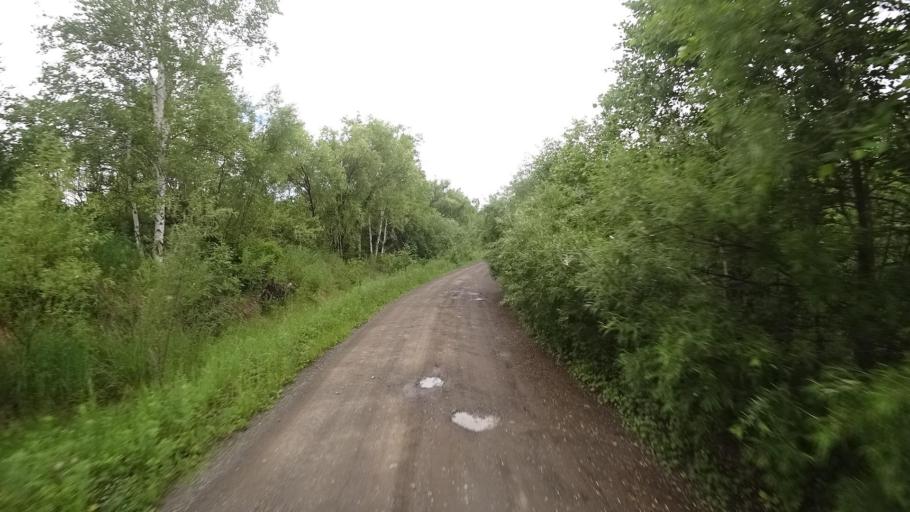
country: RU
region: Khabarovsk Krai
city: Amursk
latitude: 49.9114
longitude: 136.1579
